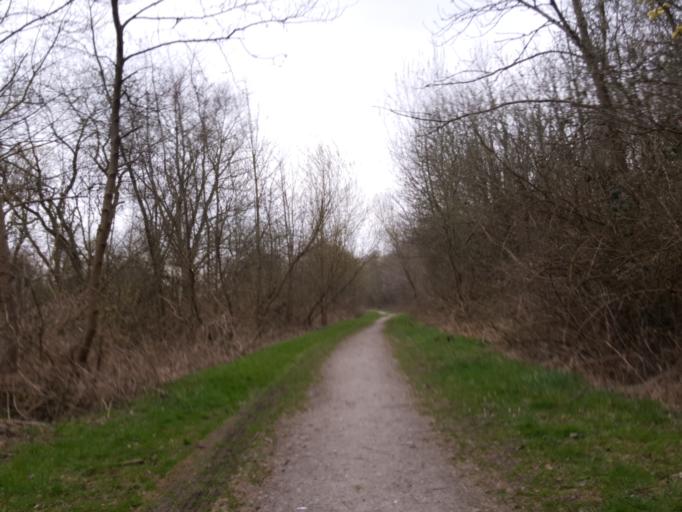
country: DE
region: Schleswig-Holstein
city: Oststeinbek
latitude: 53.5236
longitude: 10.1363
